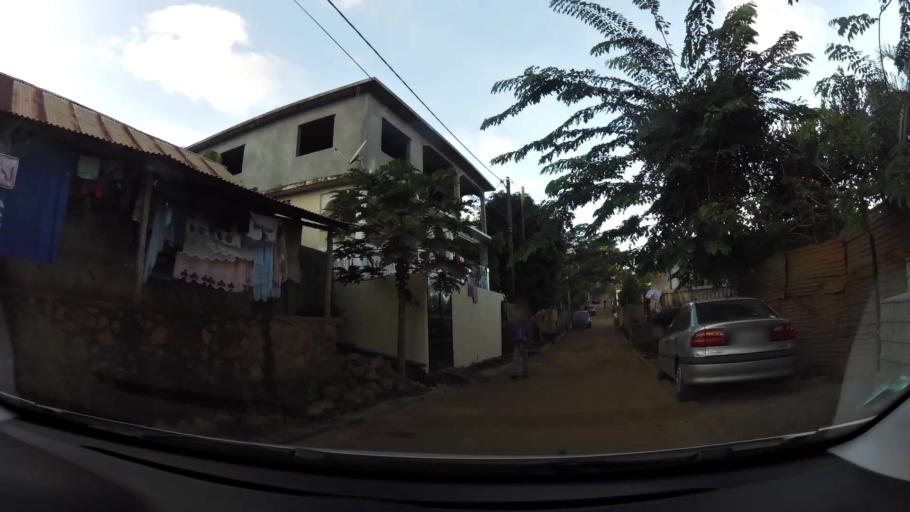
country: YT
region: Dembeni
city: Dembeni
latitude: -12.8366
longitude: 45.1744
